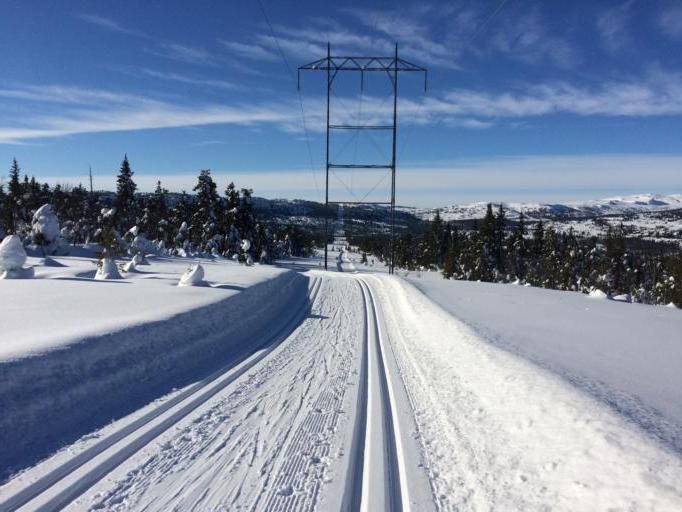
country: NO
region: Oppland
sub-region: Gausdal
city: Segalstad bru
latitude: 61.3138
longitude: 10.1058
